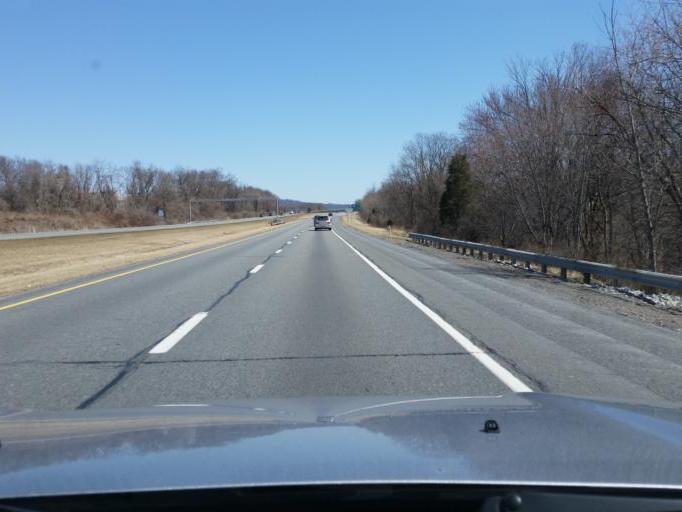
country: US
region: Pennsylvania
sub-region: Dauphin County
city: Highspire
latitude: 40.2241
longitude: -76.7710
